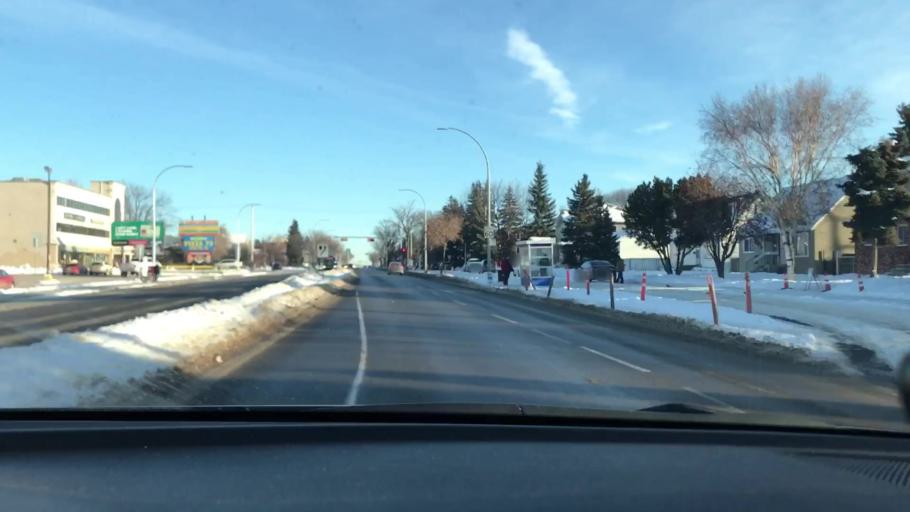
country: CA
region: Alberta
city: Edmonton
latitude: 53.5181
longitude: -113.4544
